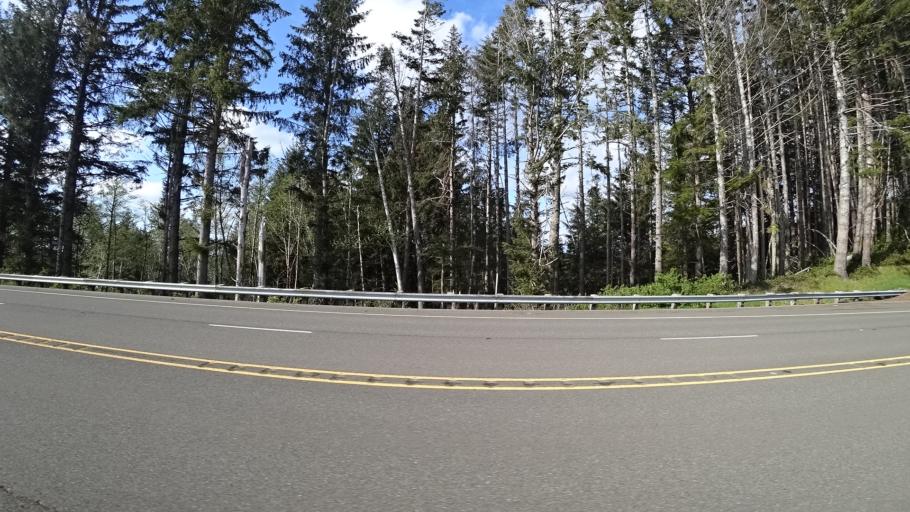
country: US
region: Oregon
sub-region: Douglas County
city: Reedsport
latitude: 43.7697
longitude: -124.1336
